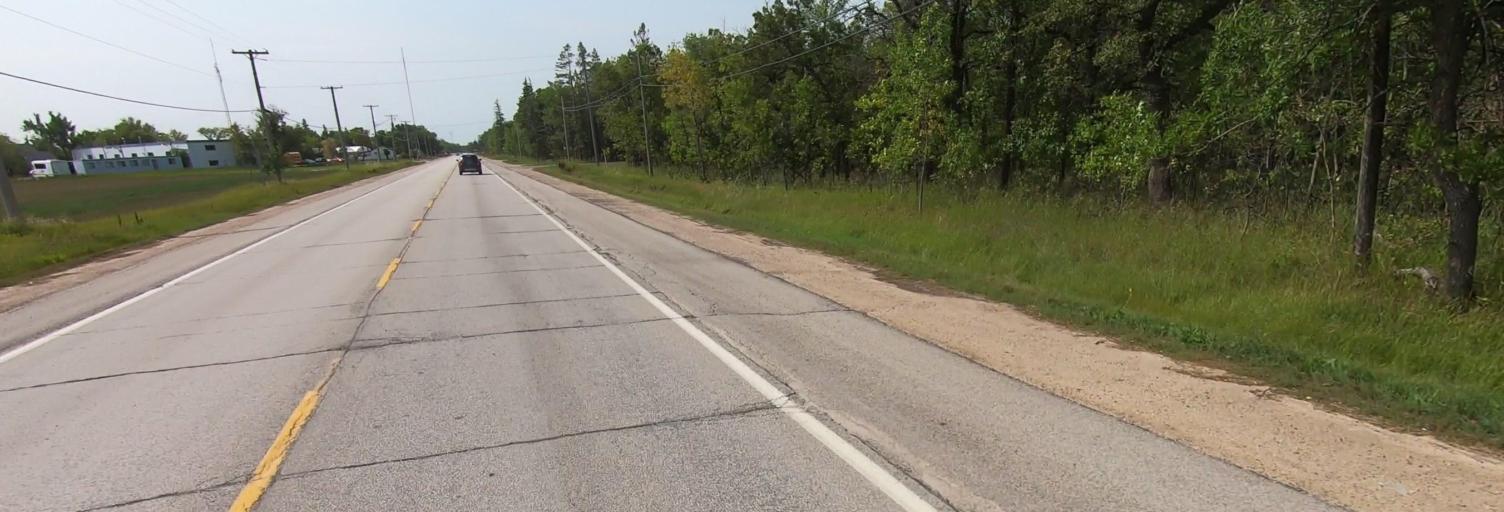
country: CA
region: Manitoba
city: Winnipeg
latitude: 49.7754
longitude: -97.1265
